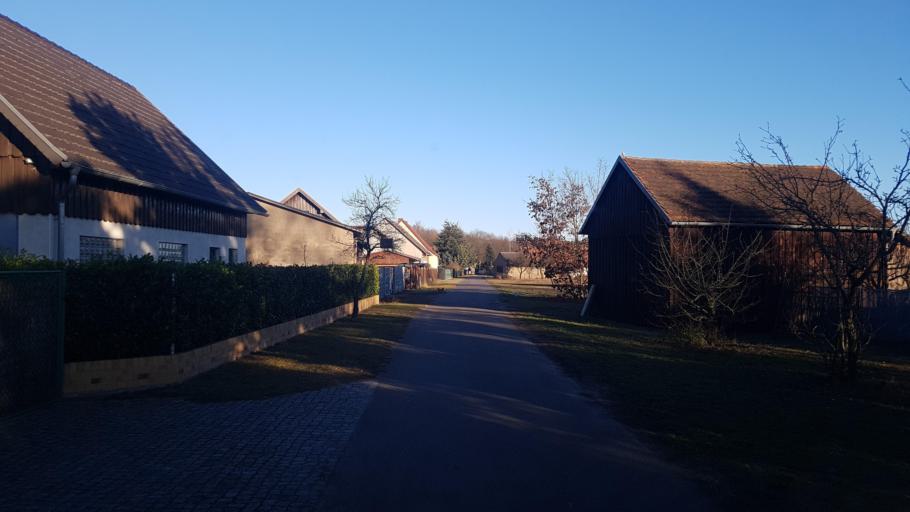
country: DE
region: Brandenburg
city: Tauer
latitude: 51.8982
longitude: 14.4639
